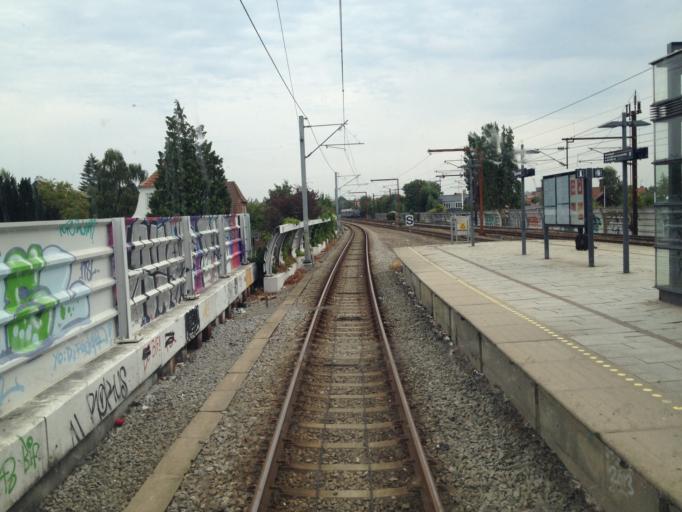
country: DK
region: Capital Region
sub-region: Kobenhavn
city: Vanlose
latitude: 55.6643
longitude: 12.4943
